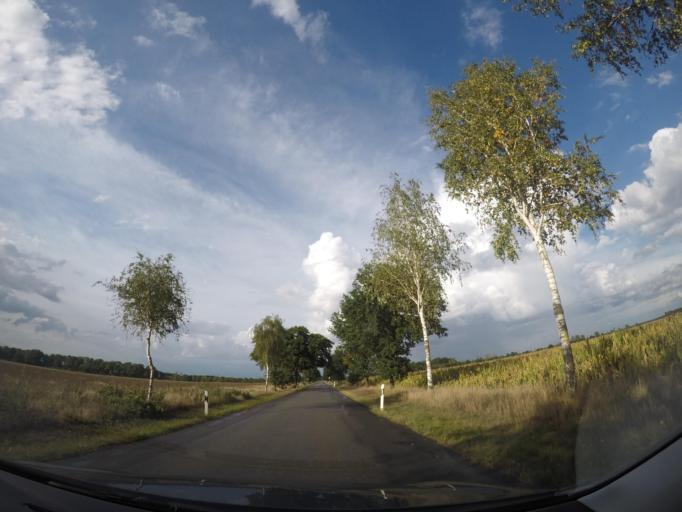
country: DE
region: Saxony-Anhalt
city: Mieste
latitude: 52.5218
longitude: 11.1482
